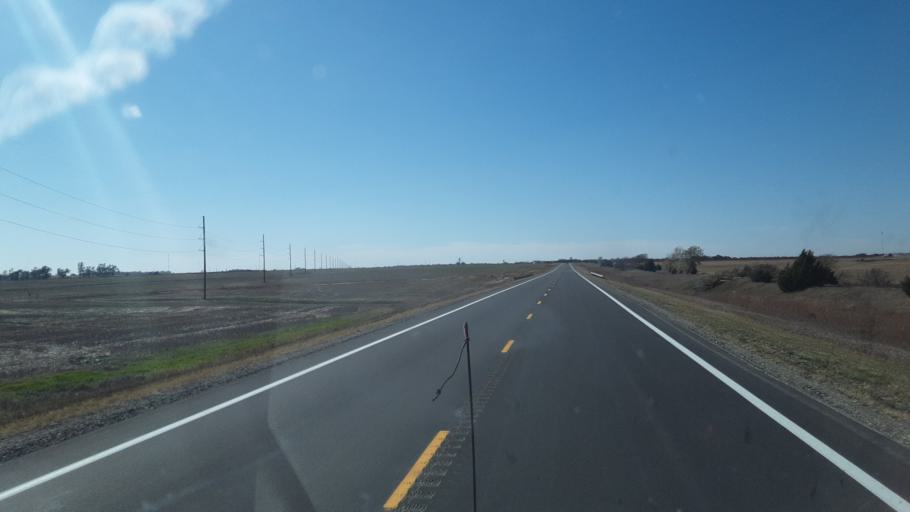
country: US
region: Kansas
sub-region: Rice County
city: Lyons
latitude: 38.3693
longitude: -98.1465
